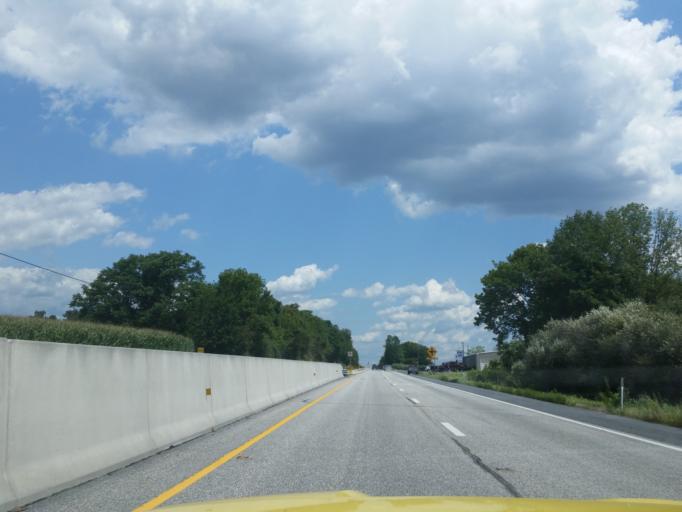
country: US
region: Pennsylvania
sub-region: Lebanon County
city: Palmyra
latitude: 40.3964
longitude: -76.6058
